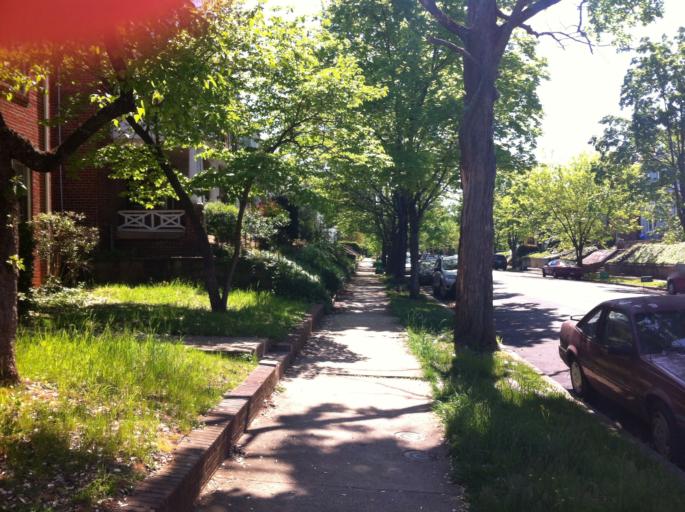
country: US
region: Virginia
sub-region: City of Richmond
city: Richmond
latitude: 37.5586
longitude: -77.4803
